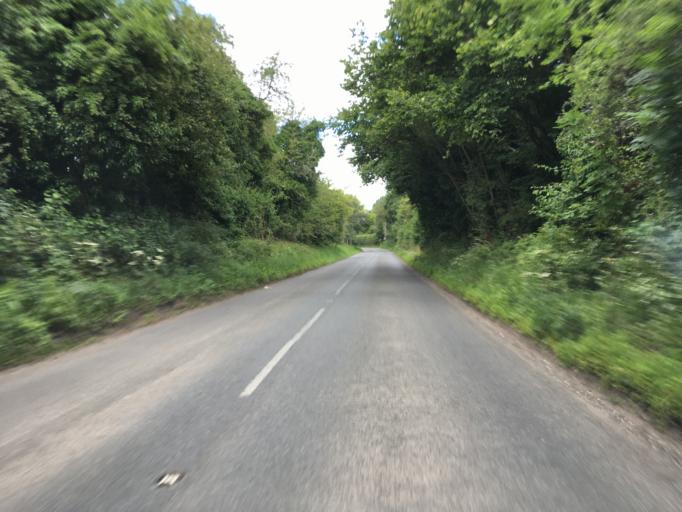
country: GB
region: England
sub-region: West Berkshire
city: Winterbourne
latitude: 51.4263
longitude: -1.3734
